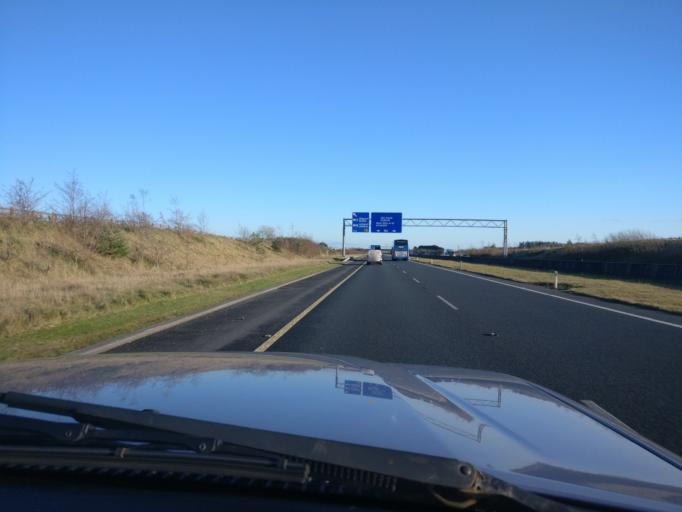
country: IE
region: Connaught
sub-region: County Galway
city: Oranmore
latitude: 53.2988
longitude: -8.8415
